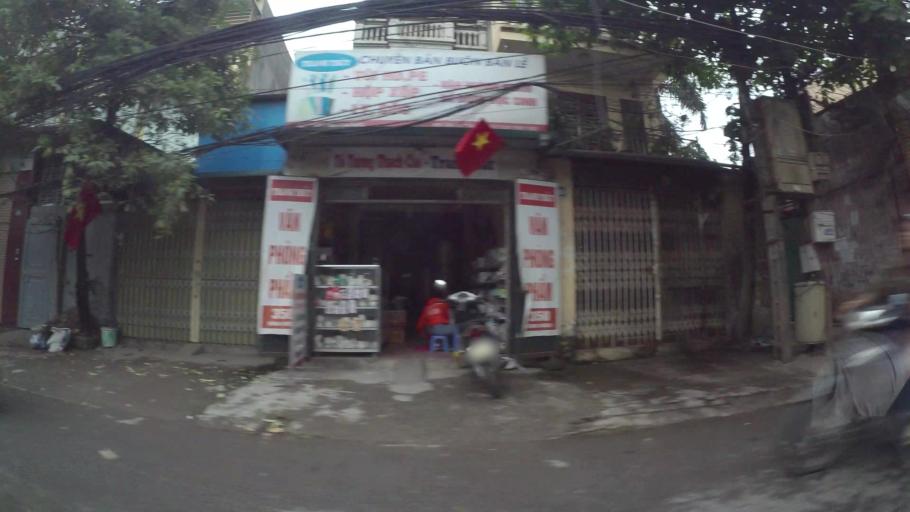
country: VN
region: Ha Noi
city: Hai BaTrung
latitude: 20.9943
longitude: 105.8800
